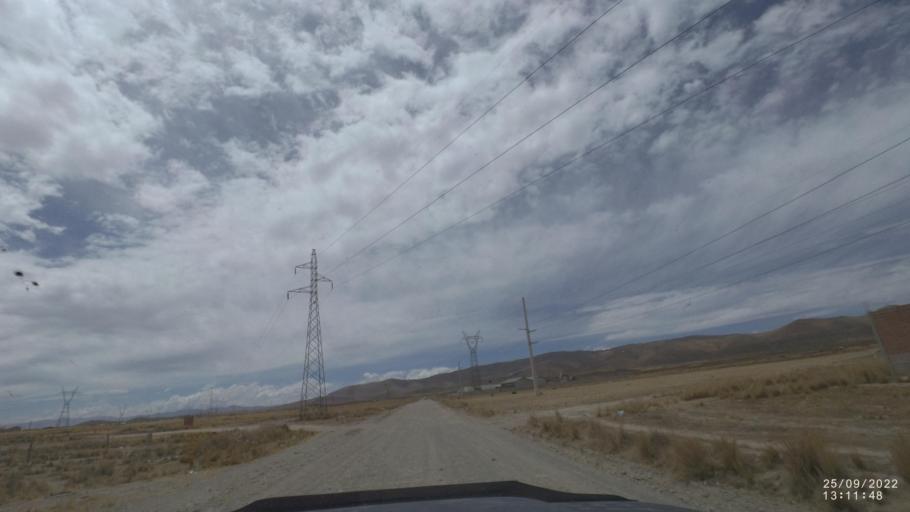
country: BO
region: Oruro
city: Oruro
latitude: -17.9621
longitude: -67.0438
